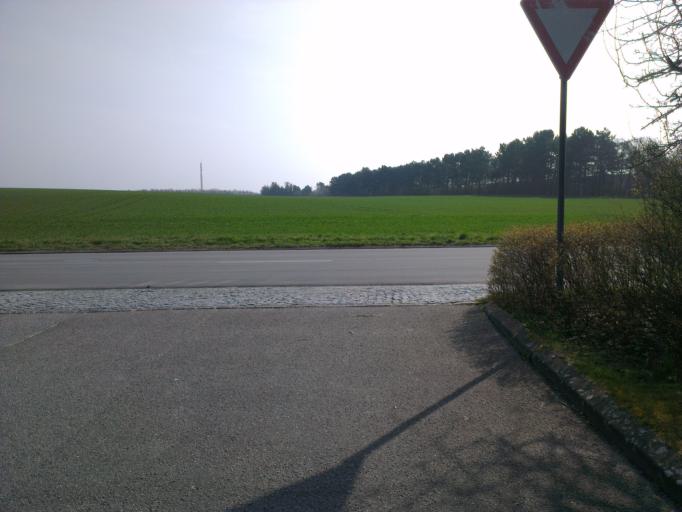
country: DK
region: Capital Region
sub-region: Frederikssund Kommune
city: Frederikssund
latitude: 55.8272
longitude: 12.0869
